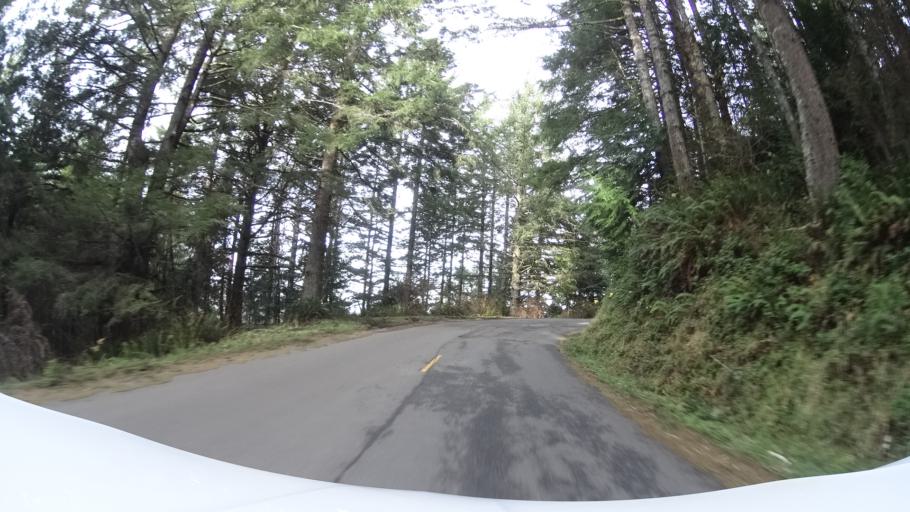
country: US
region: California
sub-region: Humboldt County
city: Ferndale
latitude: 40.5170
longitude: -124.2700
